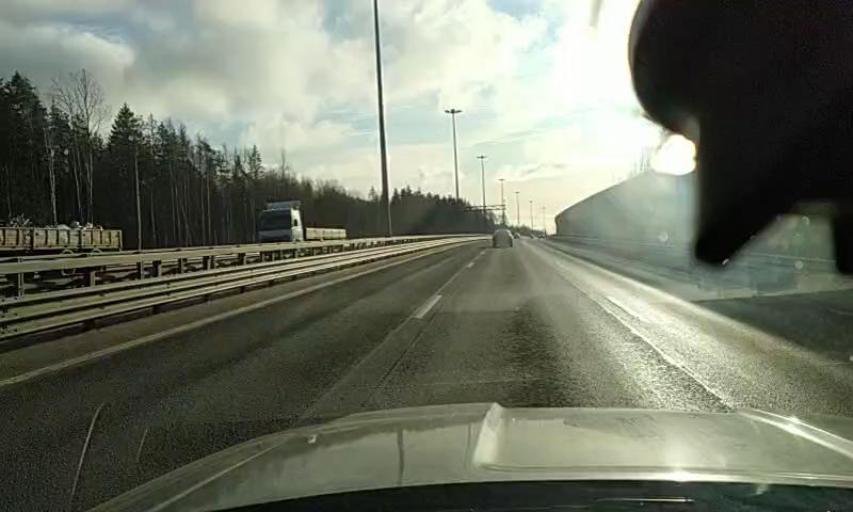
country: RU
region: St.-Petersburg
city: Beloostrov
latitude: 60.1160
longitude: 30.0773
